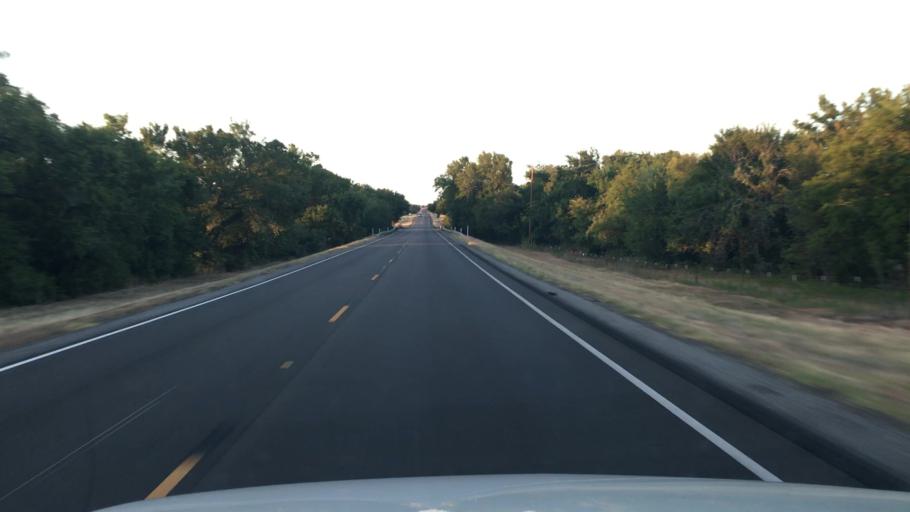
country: US
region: Texas
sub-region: Hamilton County
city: Hico
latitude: 32.0446
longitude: -98.0041
